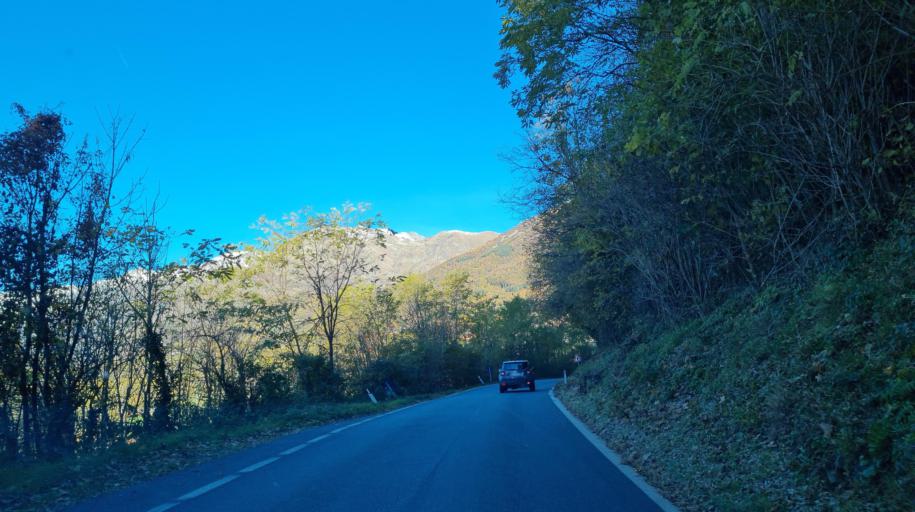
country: IT
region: Piedmont
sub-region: Provincia di Torino
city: Meugliano
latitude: 45.4849
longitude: 7.7816
